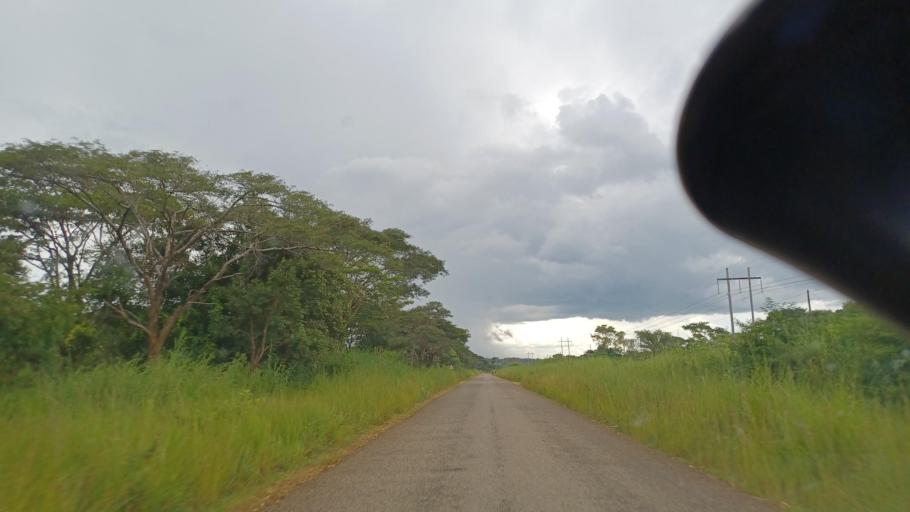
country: ZM
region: North-Western
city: Kasempa
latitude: -13.0059
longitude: 26.0102
